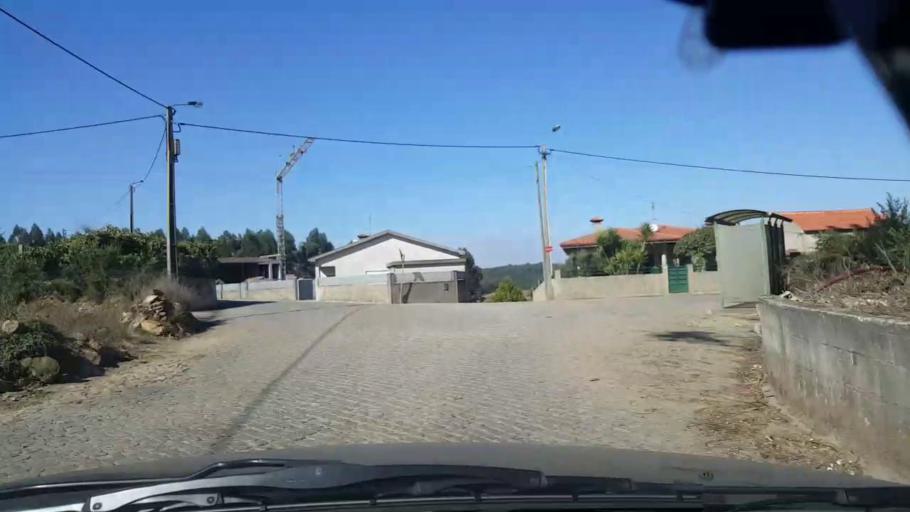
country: PT
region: Braga
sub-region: Vila Nova de Famalicao
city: Ribeirao
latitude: 41.3784
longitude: -8.6377
